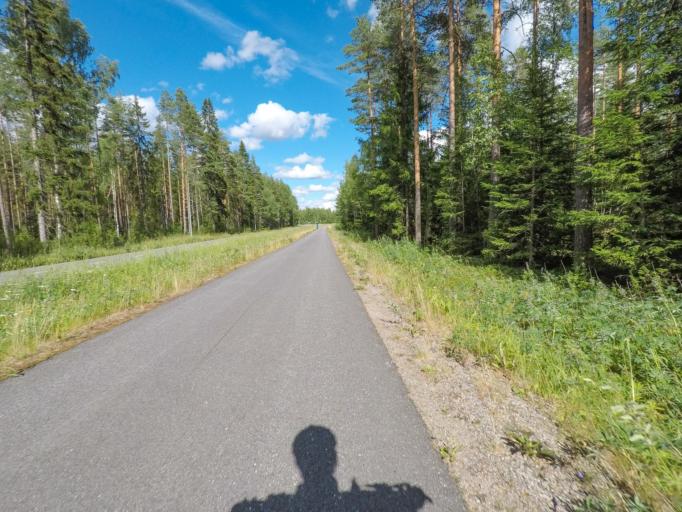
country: FI
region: South Karelia
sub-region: Lappeenranta
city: Joutseno
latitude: 61.0887
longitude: 28.3503
